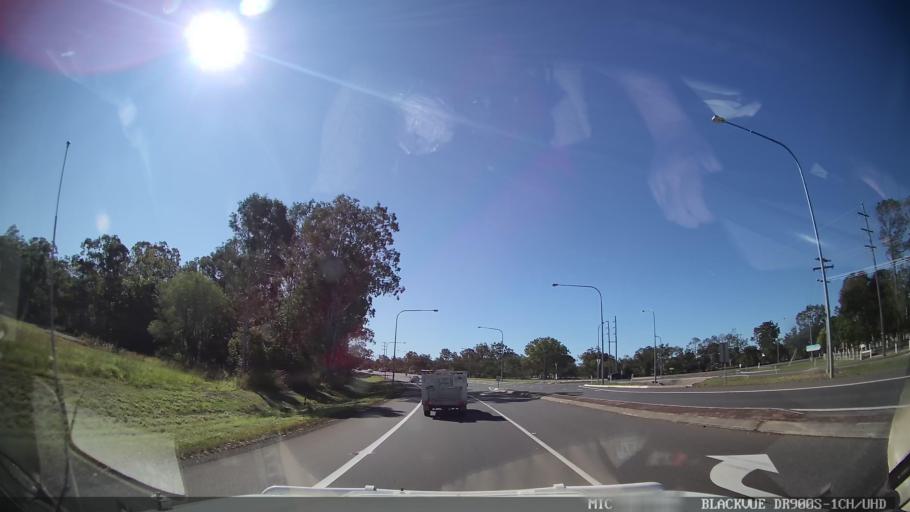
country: AU
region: Queensland
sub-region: Fraser Coast
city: Maryborough
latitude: -25.5145
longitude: 152.6708
